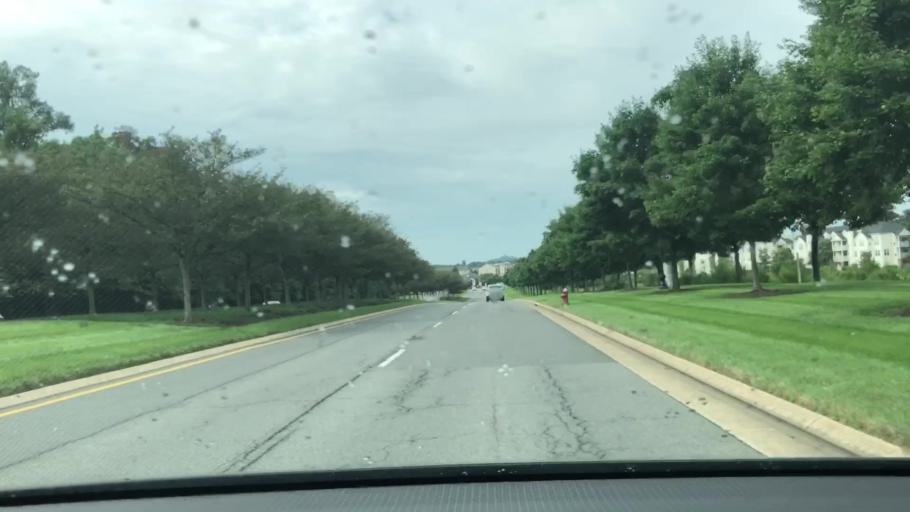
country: US
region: Virginia
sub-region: Loudoun County
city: South Riding
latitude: 38.9190
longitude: -77.5089
